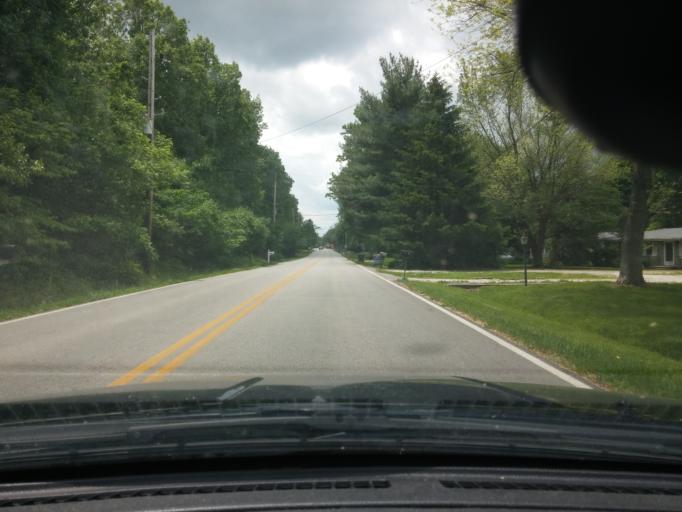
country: US
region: Indiana
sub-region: Tippecanoe County
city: West Lafayette
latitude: 40.4635
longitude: -86.9001
